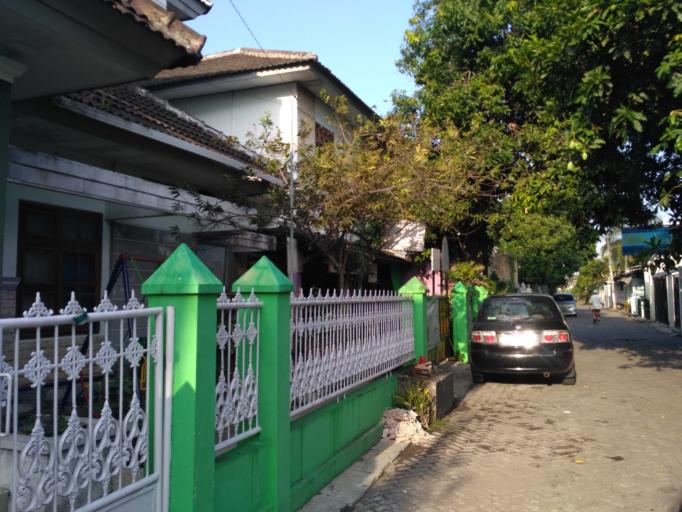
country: ID
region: Daerah Istimewa Yogyakarta
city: Yogyakarta
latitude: -7.7595
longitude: 110.3748
